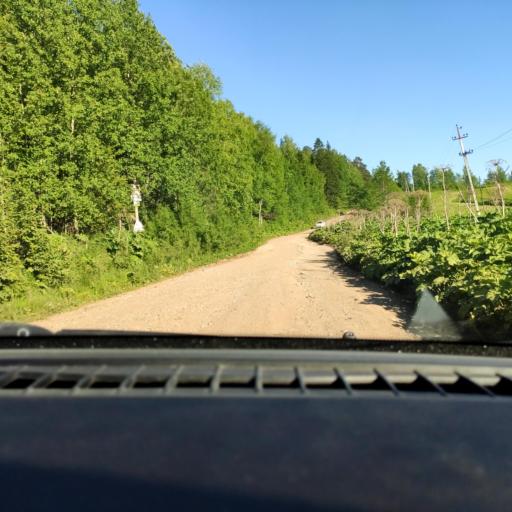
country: RU
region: Perm
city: Overyata
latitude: 58.1270
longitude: 55.8748
